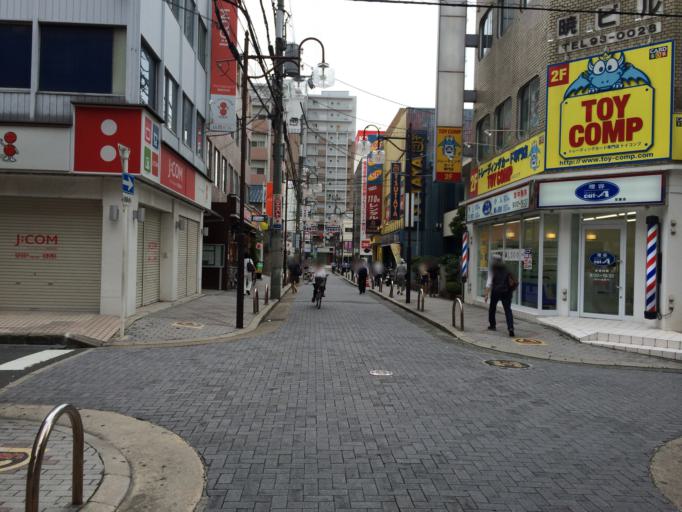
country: JP
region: Osaka
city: Ibaraki
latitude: 34.8170
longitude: 135.5780
